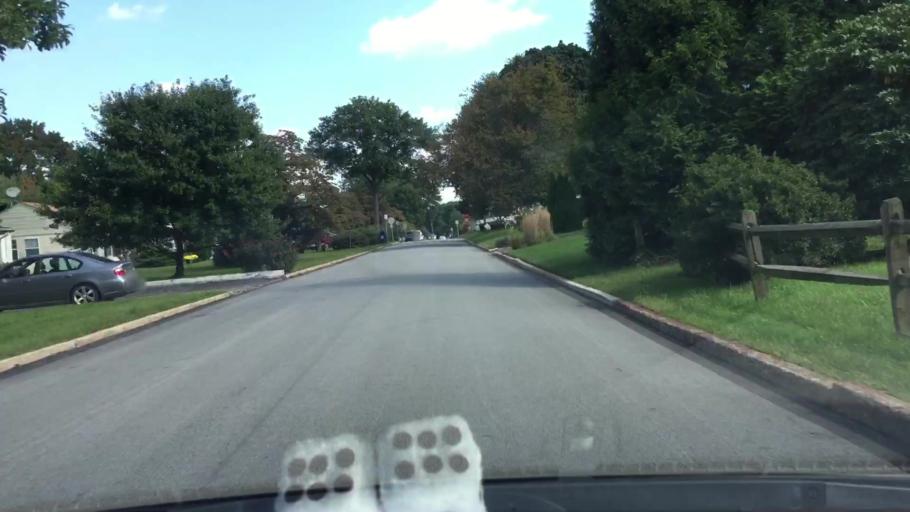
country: US
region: Pennsylvania
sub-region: Montgomery County
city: Norristown
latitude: 40.1303
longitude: -75.3052
